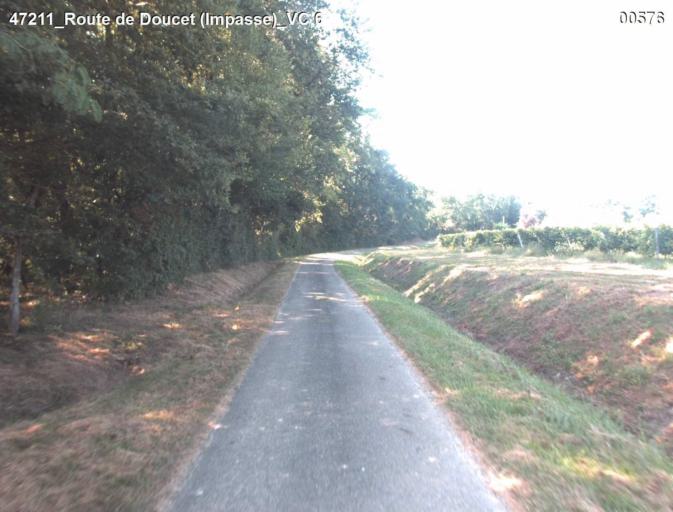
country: FR
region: Midi-Pyrenees
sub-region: Departement du Gers
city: Montreal
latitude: 44.0176
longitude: 0.2012
